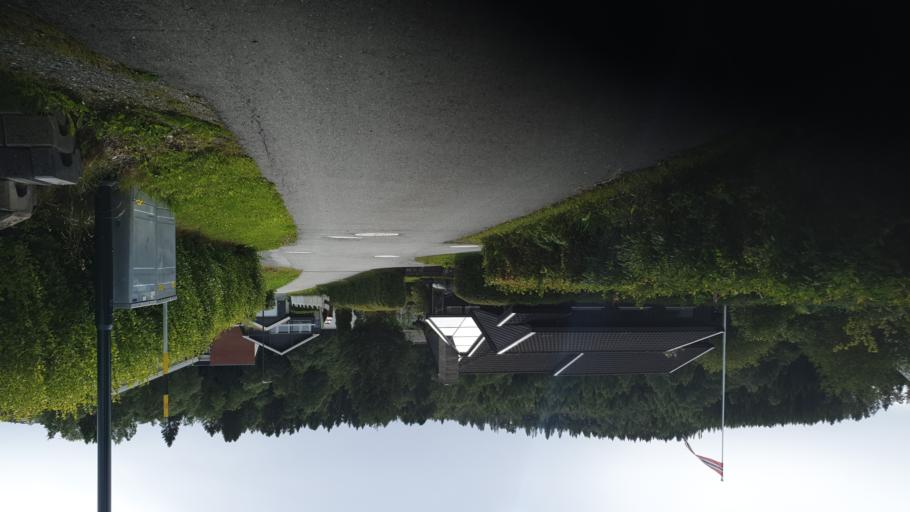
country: NO
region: Sor-Trondelag
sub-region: Malvik
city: Malvik
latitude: 63.4364
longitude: 10.6595
